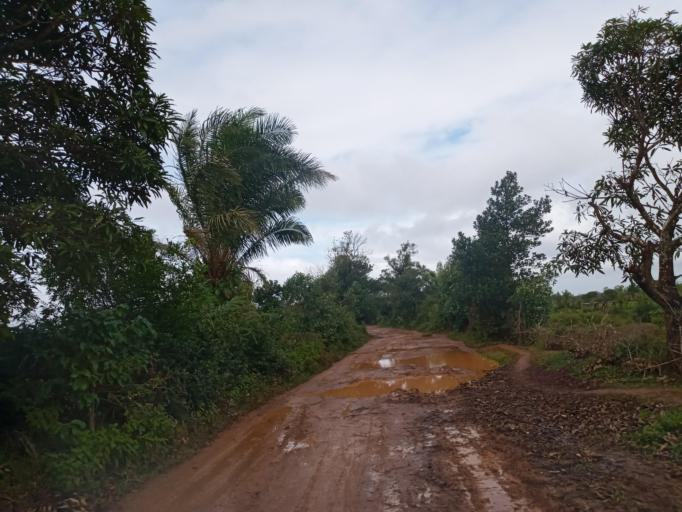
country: MG
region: Atsimo-Atsinanana
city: Vohipaho
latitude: -23.7942
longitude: 47.5425
